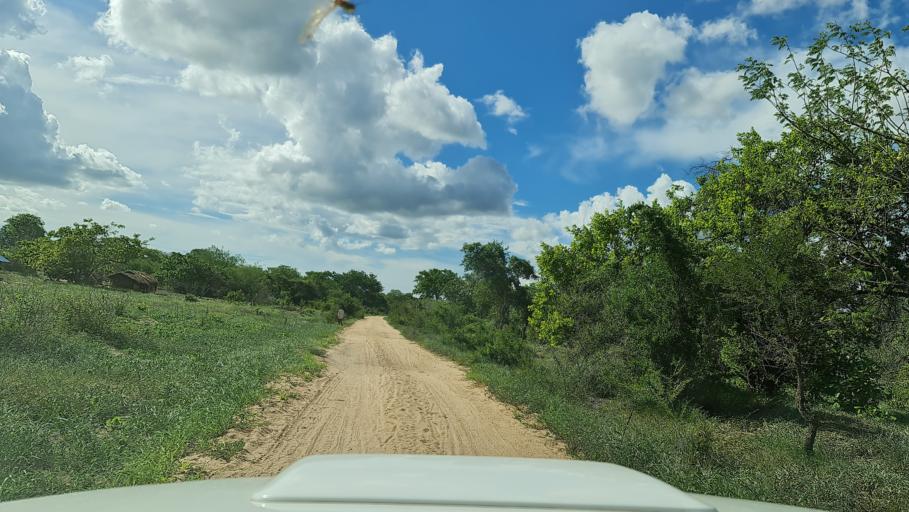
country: MZ
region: Nampula
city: Ilha de Mocambique
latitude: -15.4041
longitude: 40.2397
